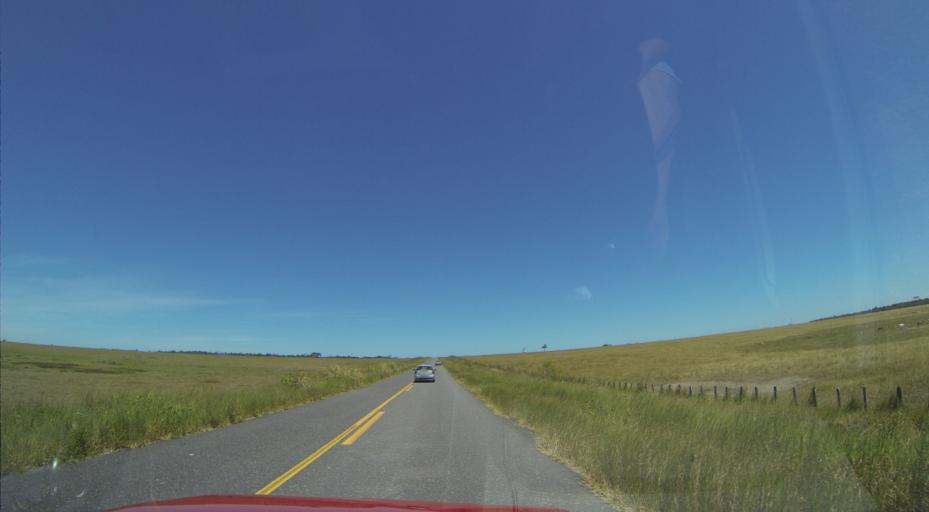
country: BR
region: Bahia
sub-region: Prado
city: Prado
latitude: -17.2335
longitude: -39.3703
